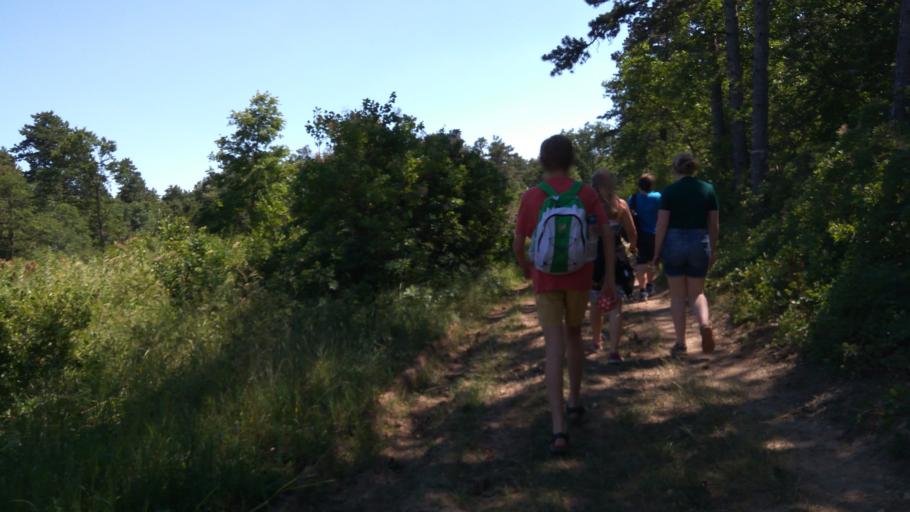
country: HU
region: Veszprem
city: Balatonfured
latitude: 46.9925
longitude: 17.8767
